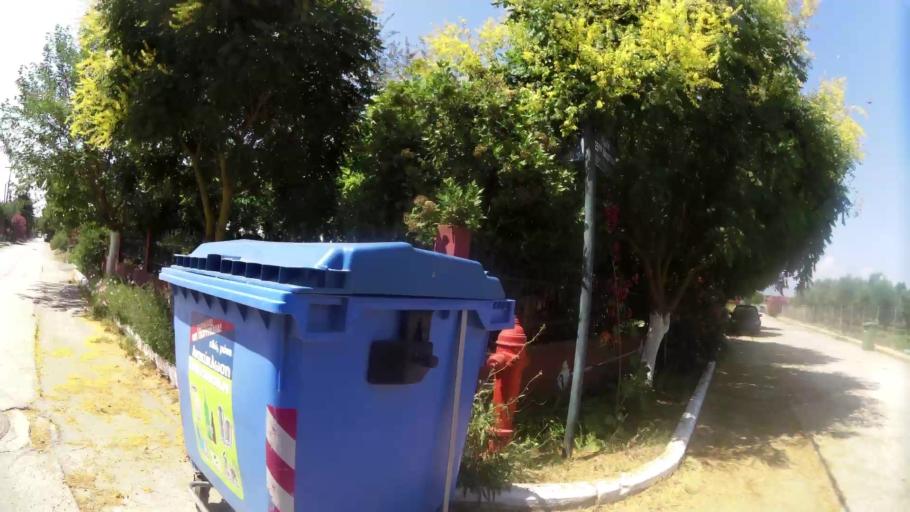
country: GR
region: Central Macedonia
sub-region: Nomos Thessalonikis
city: Agia Triada
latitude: 40.4991
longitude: 22.8363
